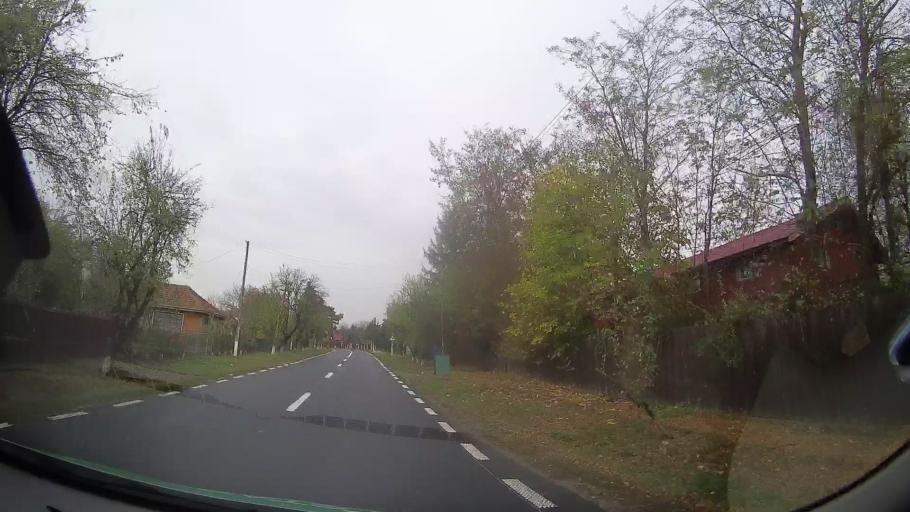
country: RO
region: Ilfov
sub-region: Comuna Nuci
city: Nuci
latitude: 44.7219
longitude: 26.2953
